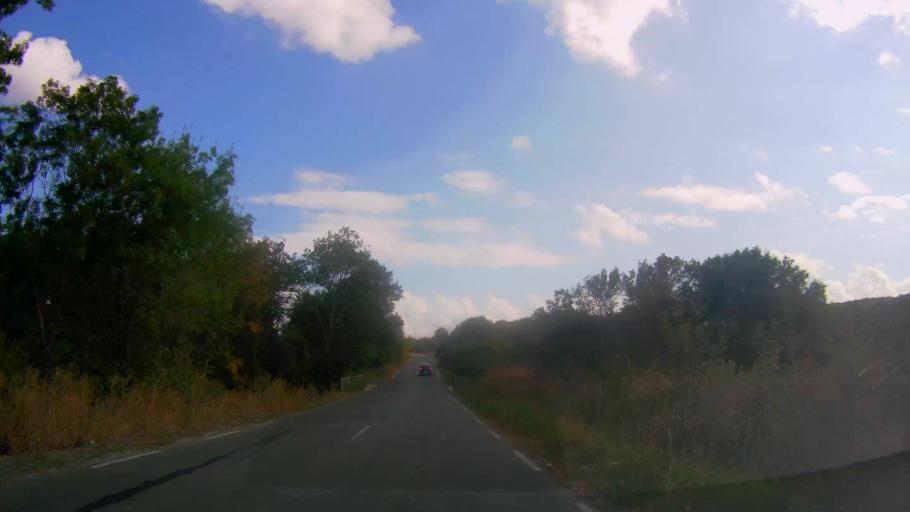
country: BG
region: Burgas
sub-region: Obshtina Kameno
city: Kameno
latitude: 42.4815
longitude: 27.3455
